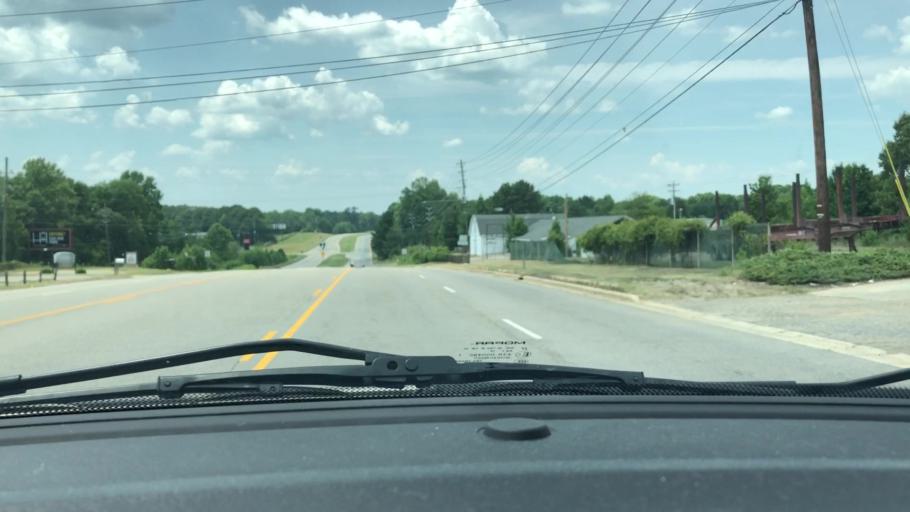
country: US
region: North Carolina
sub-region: Lee County
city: Sanford
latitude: 35.4978
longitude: -79.1990
